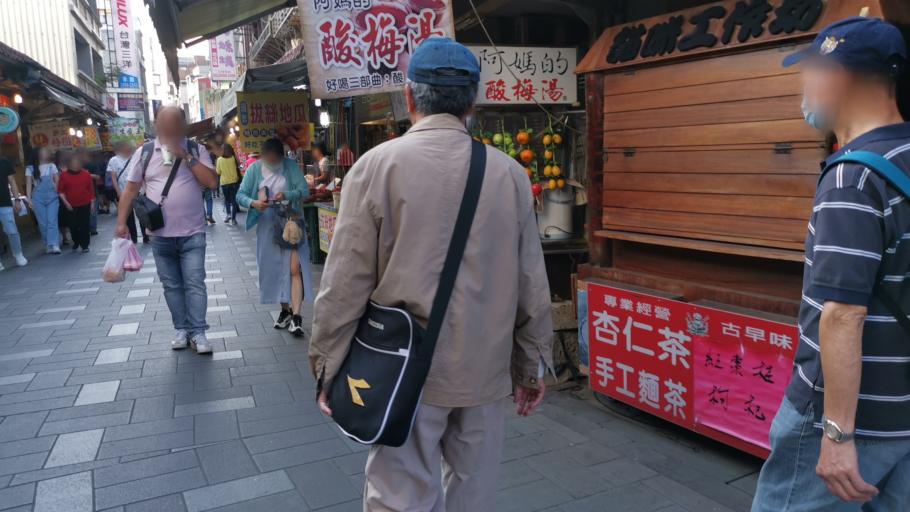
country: TW
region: Taiwan
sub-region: Keelung
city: Keelung
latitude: 25.2208
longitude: 121.6398
